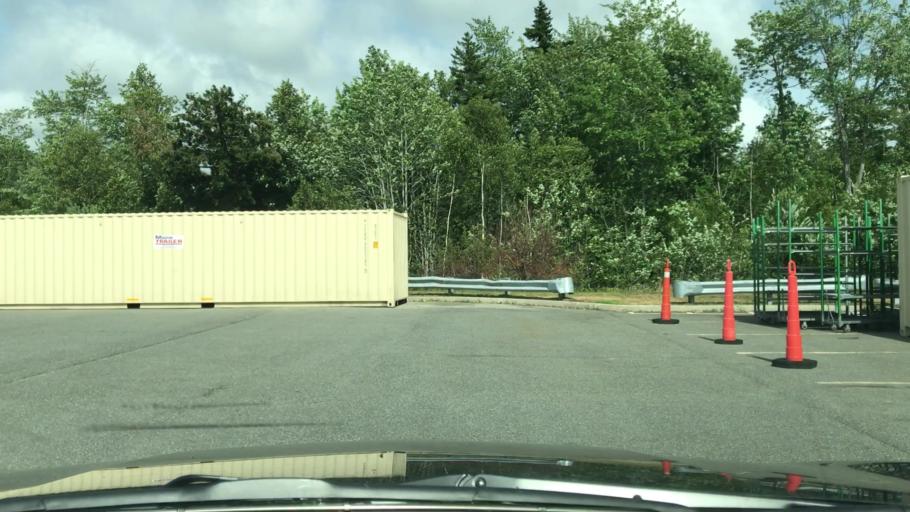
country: US
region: Maine
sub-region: Hancock County
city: Ellsworth
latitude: 44.5238
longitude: -68.3920
